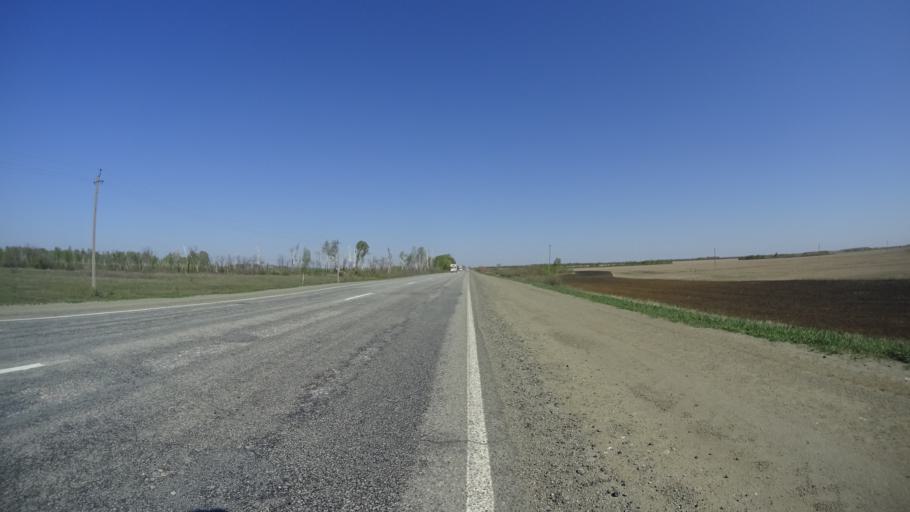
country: RU
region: Chelyabinsk
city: Troitsk
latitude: 54.1937
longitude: 61.4331
